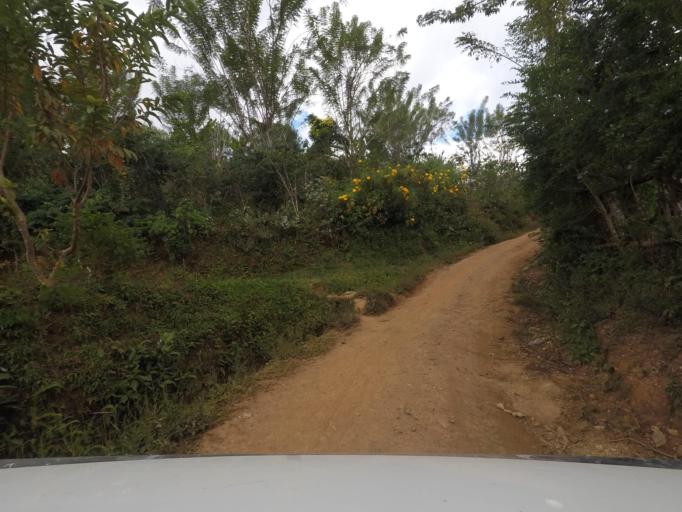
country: TL
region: Ermera
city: Gleno
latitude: -8.7219
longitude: 125.3252
